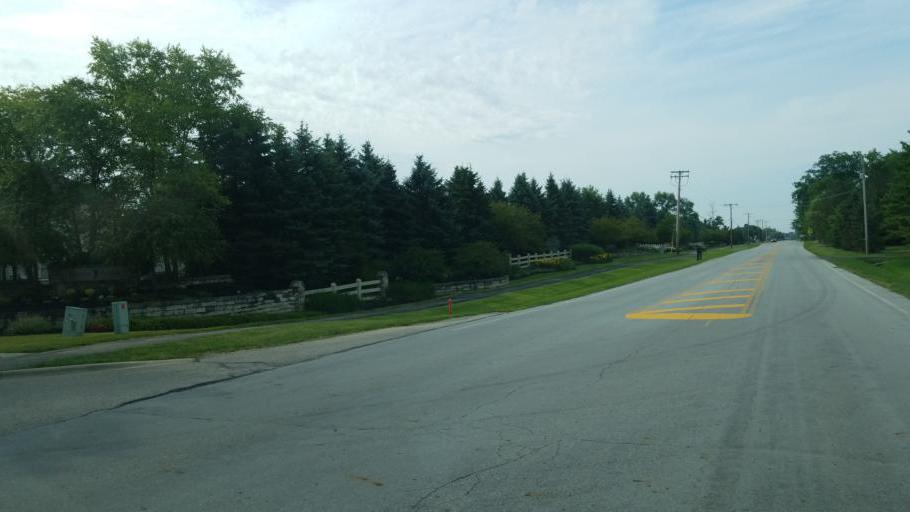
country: US
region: Ohio
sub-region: Franklin County
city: Dublin
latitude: 40.1647
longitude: -83.1546
